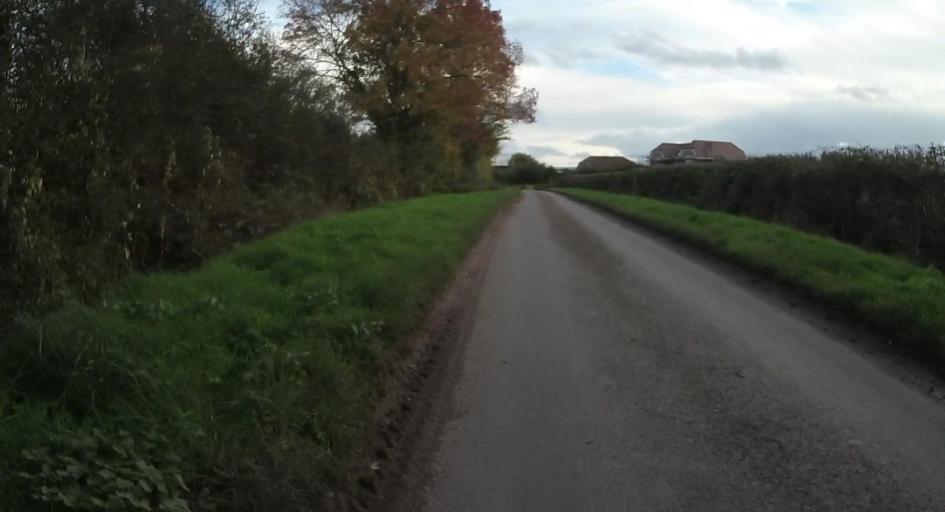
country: GB
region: England
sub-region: Wokingham
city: Swallowfield
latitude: 51.3715
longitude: -0.9596
